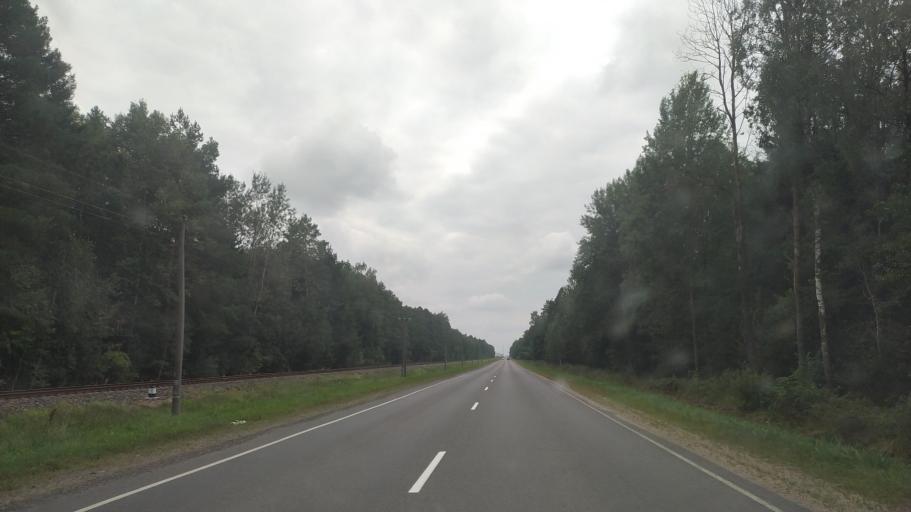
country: BY
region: Brest
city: Byelaazyorsk
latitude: 52.5349
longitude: 25.1415
